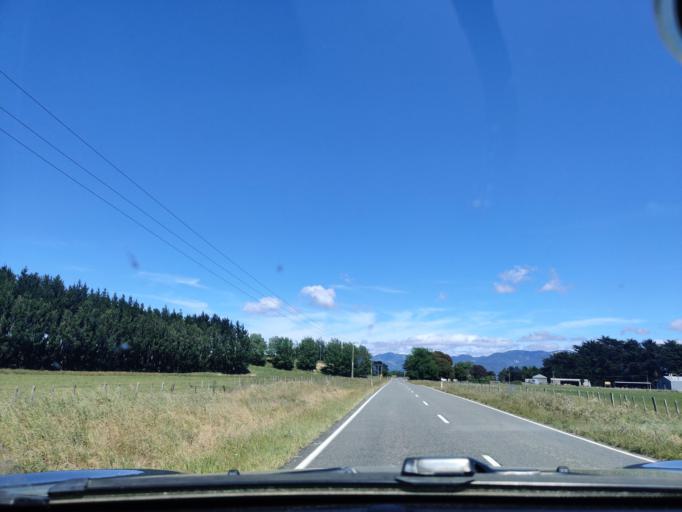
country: NZ
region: Wellington
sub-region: Upper Hutt City
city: Upper Hutt
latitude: -41.3279
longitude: 175.2168
